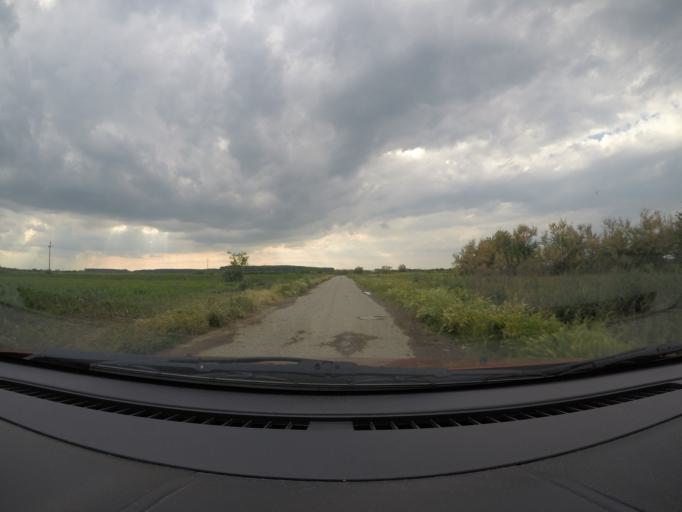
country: RS
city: Uzdin
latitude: 45.2036
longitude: 20.6066
